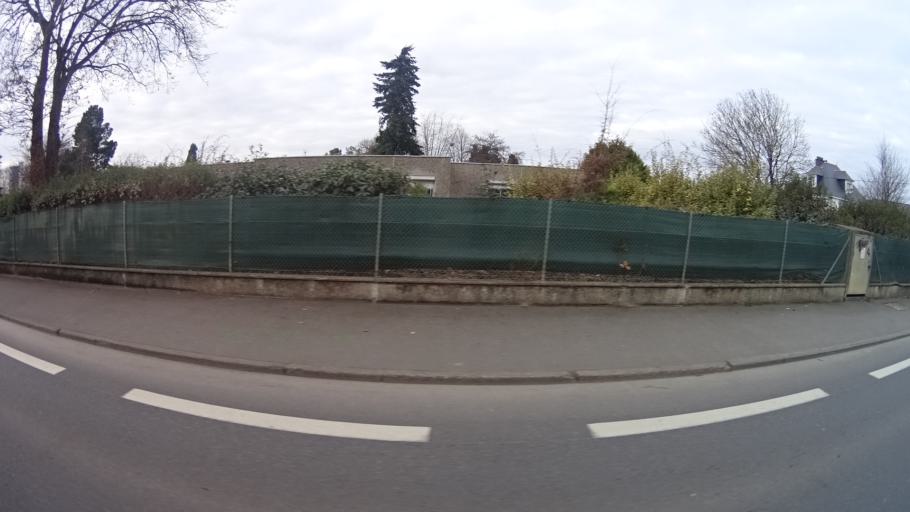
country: FR
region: Brittany
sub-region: Departement d'Ille-et-Vilaine
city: Redon
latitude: 47.6621
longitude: -2.0717
